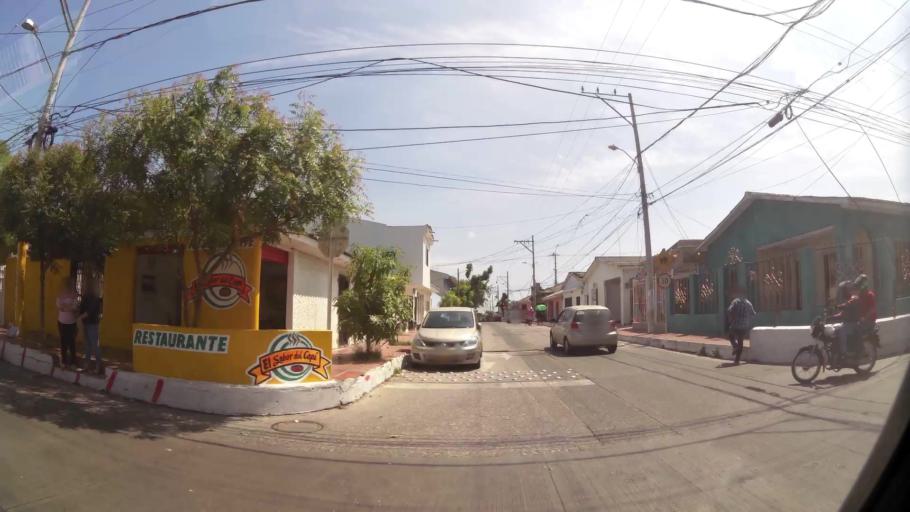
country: CO
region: Atlantico
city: Barranquilla
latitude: 10.9631
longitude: -74.8051
